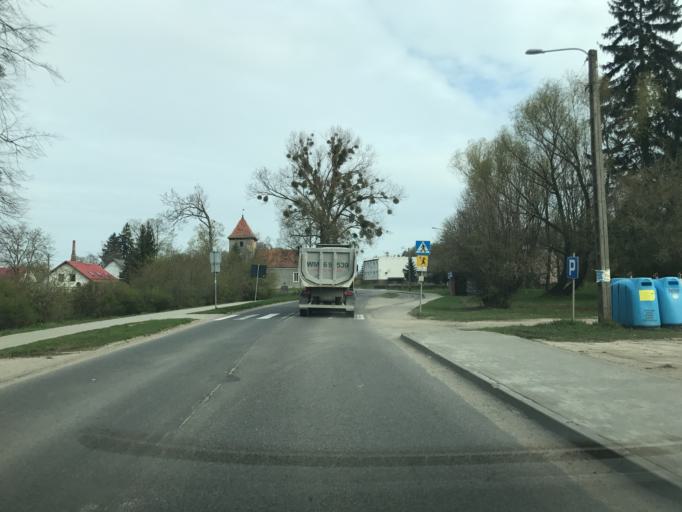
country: PL
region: Warmian-Masurian Voivodeship
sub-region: Powiat ostrodzki
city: Gierzwald
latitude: 53.5412
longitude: 20.0889
